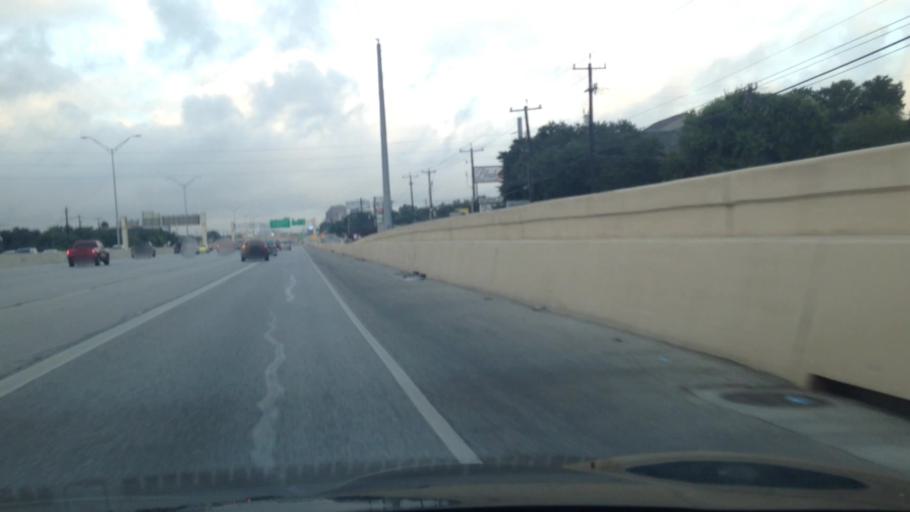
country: US
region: Texas
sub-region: Bexar County
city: Windcrest
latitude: 29.5166
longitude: -98.4144
